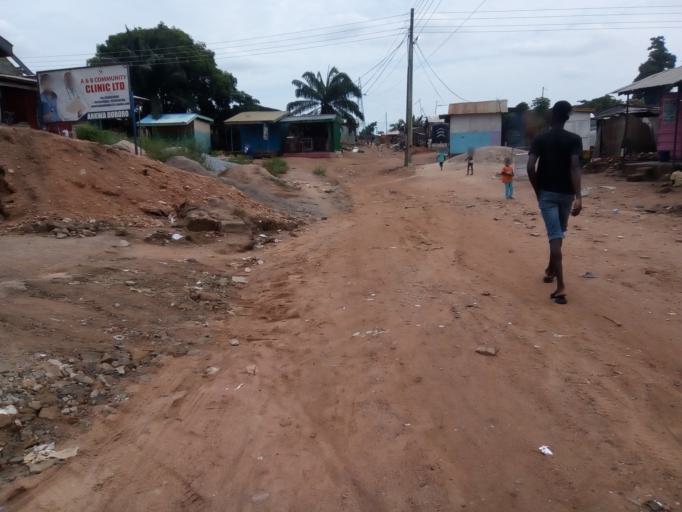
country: GH
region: Eastern
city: Nsawam
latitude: 5.7791
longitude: -0.3356
